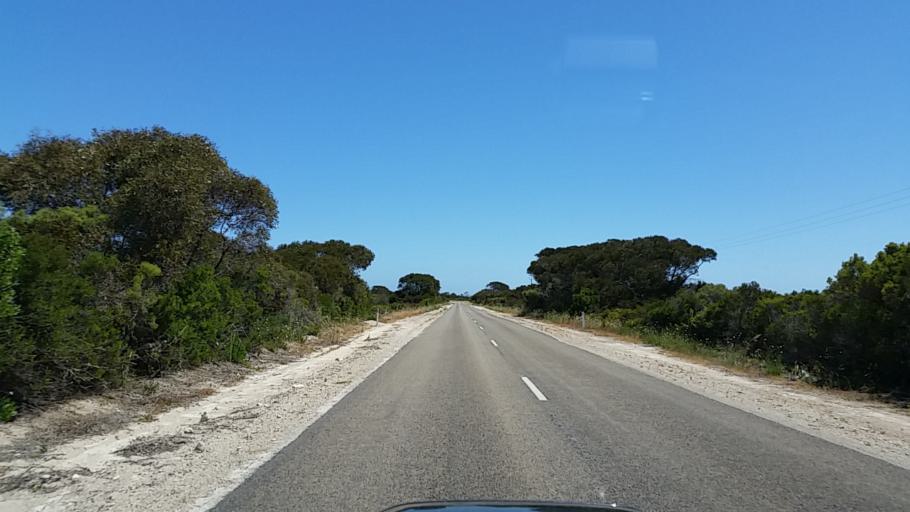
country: AU
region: South Australia
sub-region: Yorke Peninsula
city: Honiton
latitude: -35.2199
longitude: 136.9980
